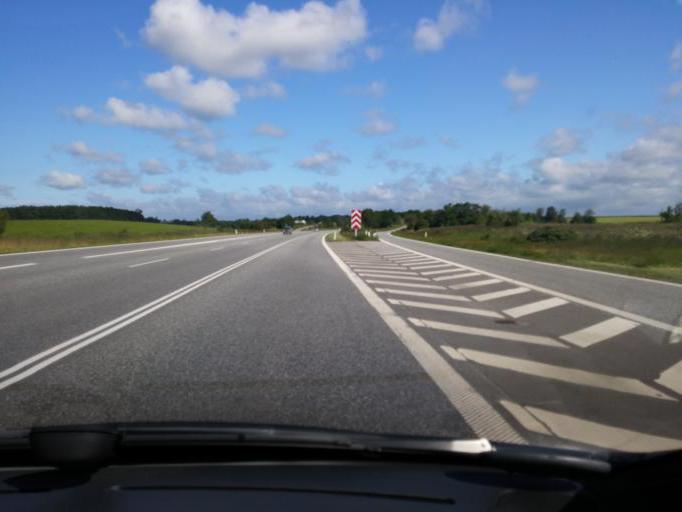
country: DK
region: Capital Region
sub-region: Hillerod Kommune
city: Hillerod
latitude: 55.9021
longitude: 12.2727
